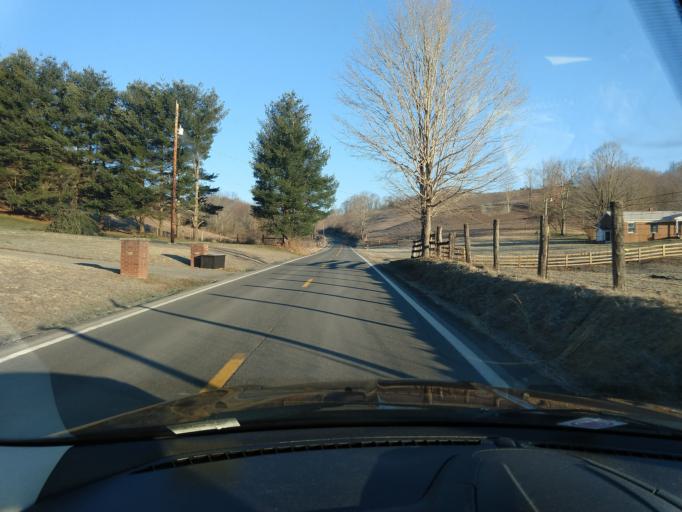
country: US
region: West Virginia
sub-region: Greenbrier County
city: Rainelle
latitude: 37.8669
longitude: -80.7226
